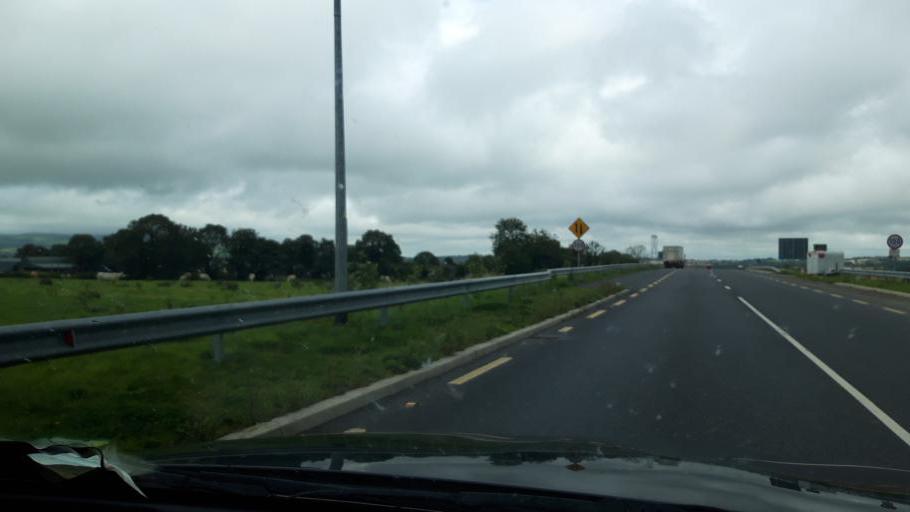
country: IE
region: Leinster
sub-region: Loch Garman
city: New Ross
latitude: 52.4190
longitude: -6.8598
